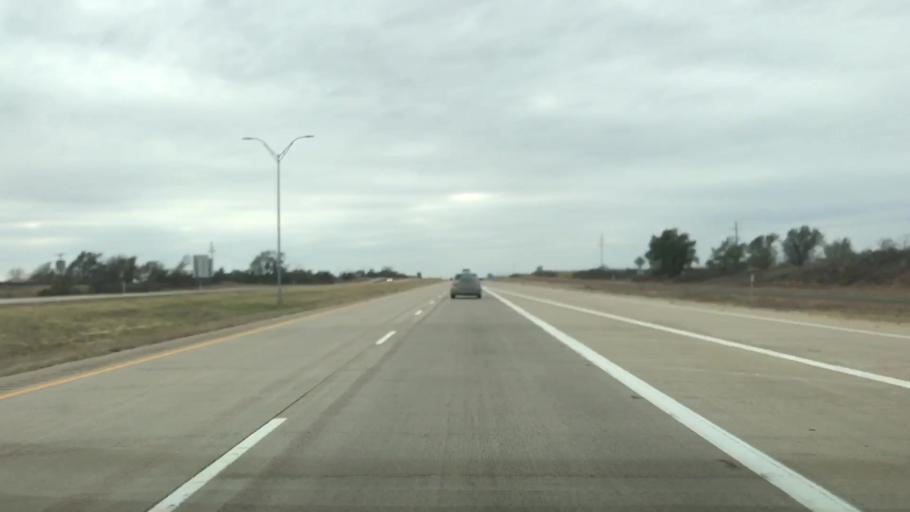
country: US
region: Texas
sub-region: Wheeler County
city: Shamrock
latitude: 35.2272
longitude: -100.1721
